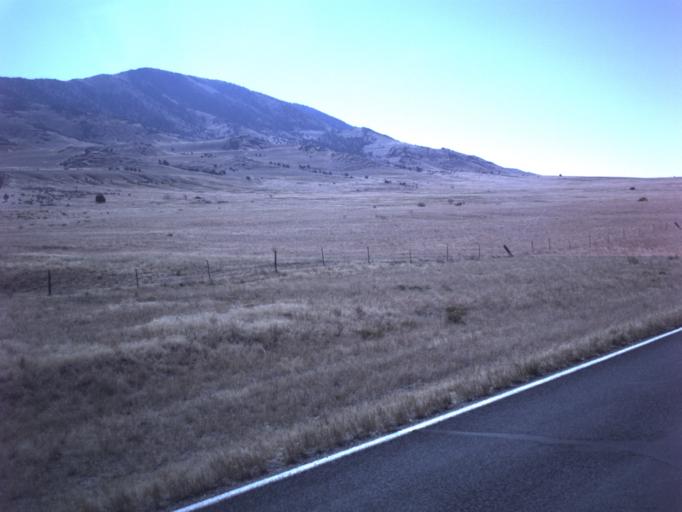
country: US
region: Utah
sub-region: Tooele County
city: Grantsville
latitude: 40.5749
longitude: -112.7284
